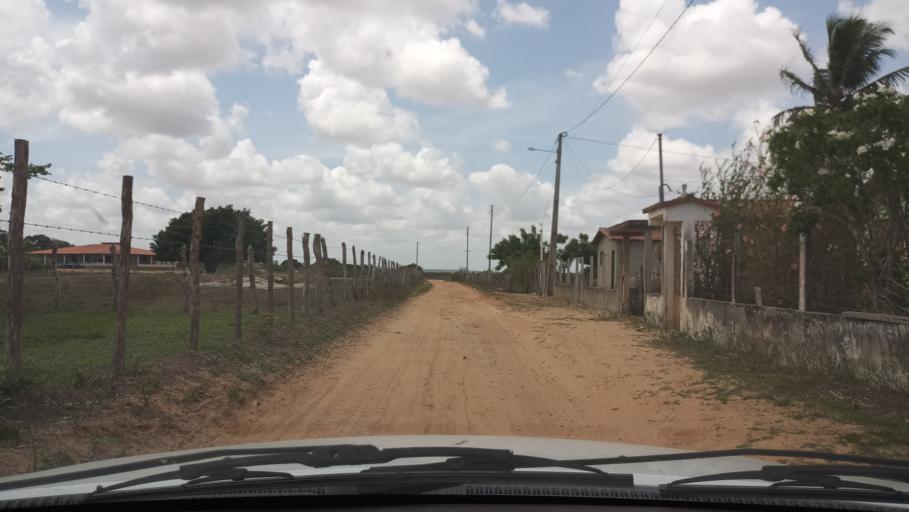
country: BR
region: Rio Grande do Norte
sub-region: Brejinho
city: Brejinho
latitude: -6.2754
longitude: -35.3473
